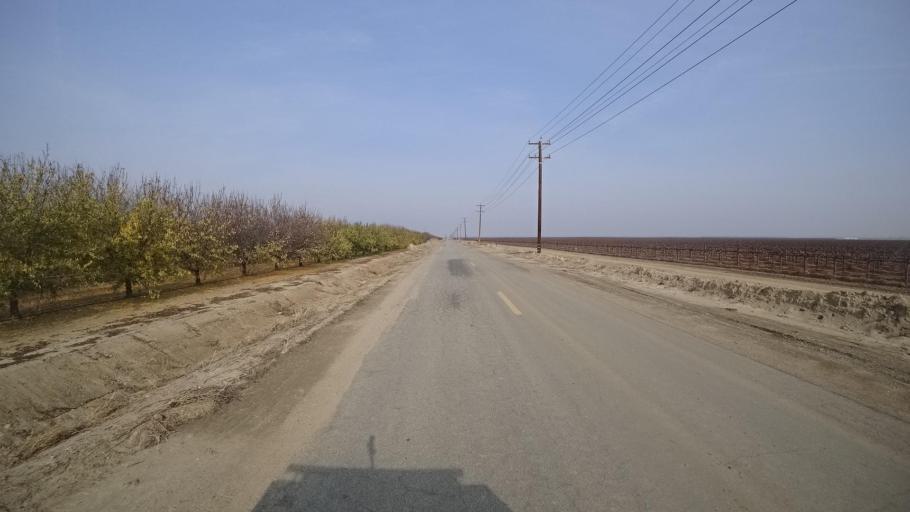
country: US
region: California
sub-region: Kern County
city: Greenfield
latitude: 35.0810
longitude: -119.1006
